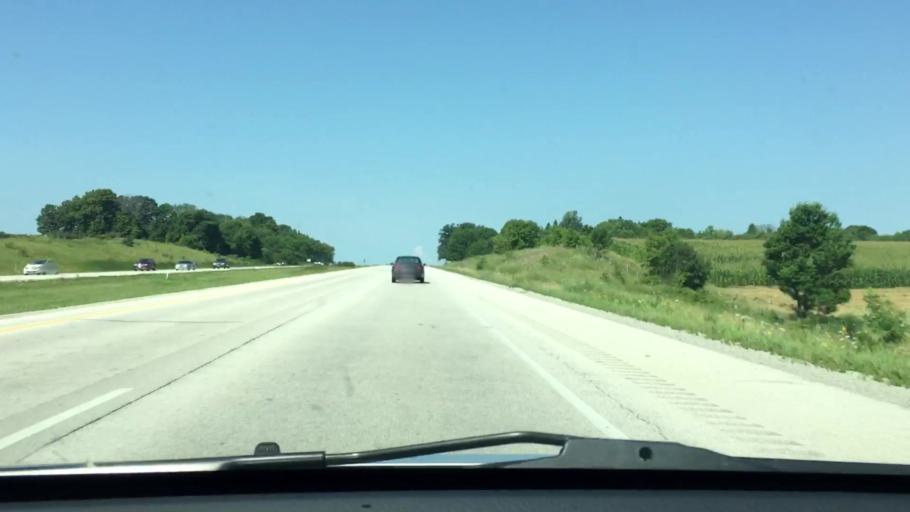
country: US
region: Wisconsin
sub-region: Jefferson County
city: Ixonia
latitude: 43.0849
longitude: -88.6500
